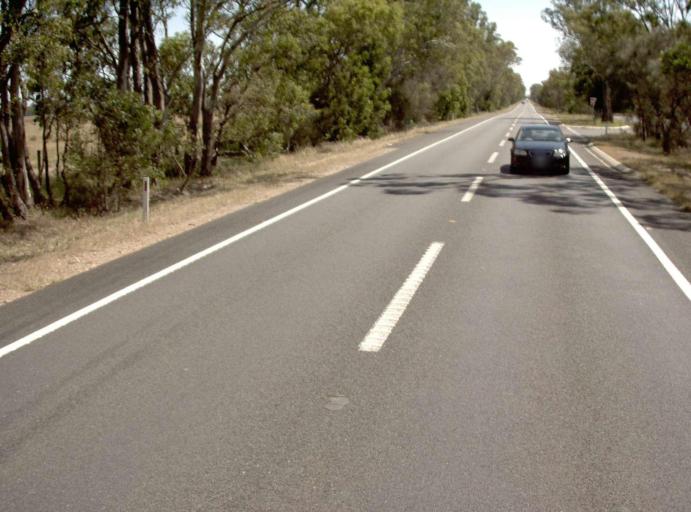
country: AU
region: Victoria
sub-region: Wellington
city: Sale
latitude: -37.9487
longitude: 147.1164
